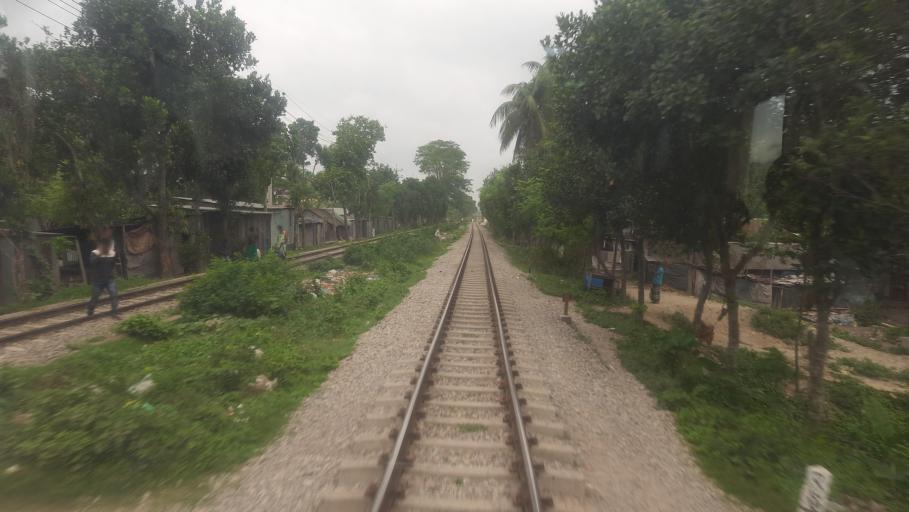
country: BD
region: Dhaka
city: Narsingdi
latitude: 23.9315
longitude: 90.7321
